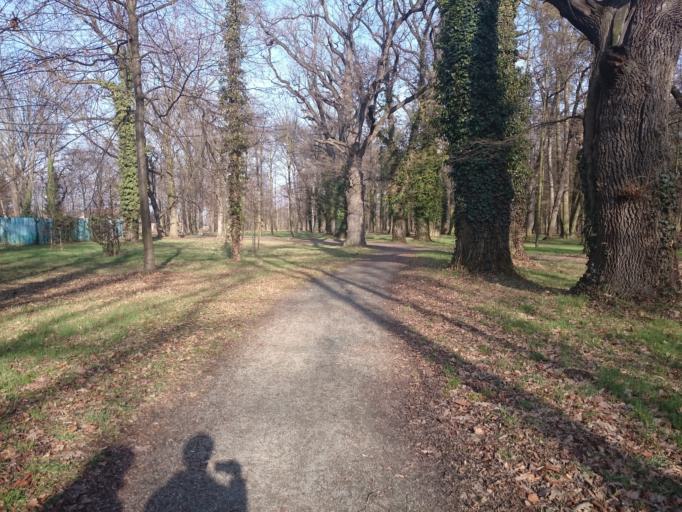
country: CZ
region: Pardubicky
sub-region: Okres Chrudim
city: Hermanuv Mestec
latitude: 49.9487
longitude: 15.6748
